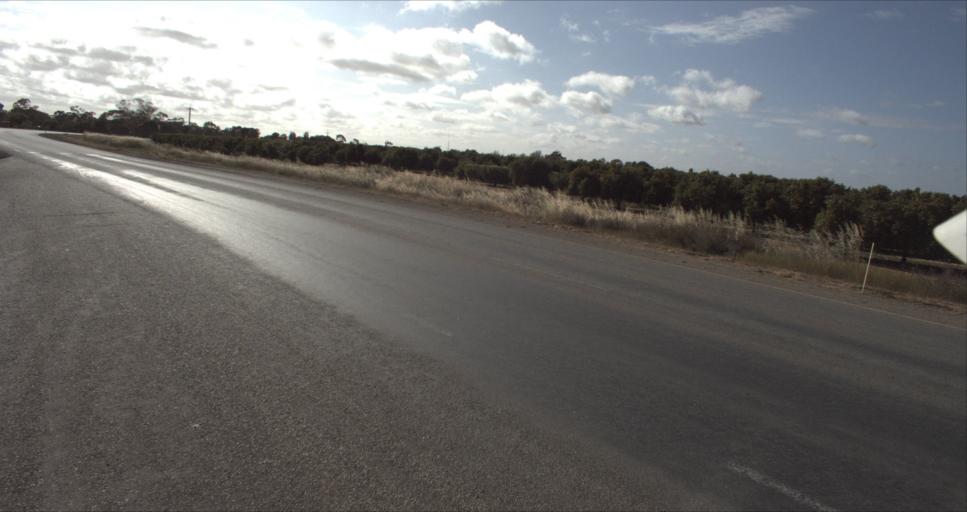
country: AU
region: New South Wales
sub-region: Leeton
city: Leeton
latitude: -34.5708
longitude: 146.4045
